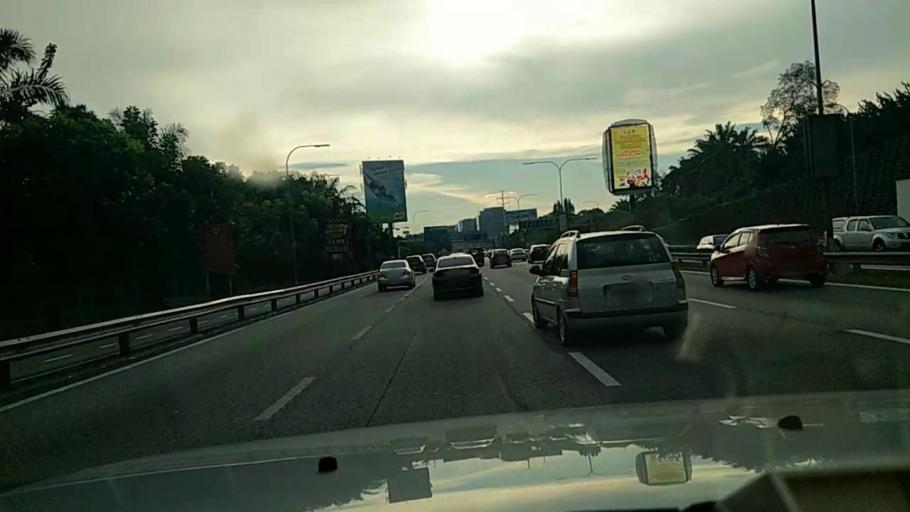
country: MY
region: Selangor
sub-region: Petaling
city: Petaling Jaya
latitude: 3.0834
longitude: 101.5998
